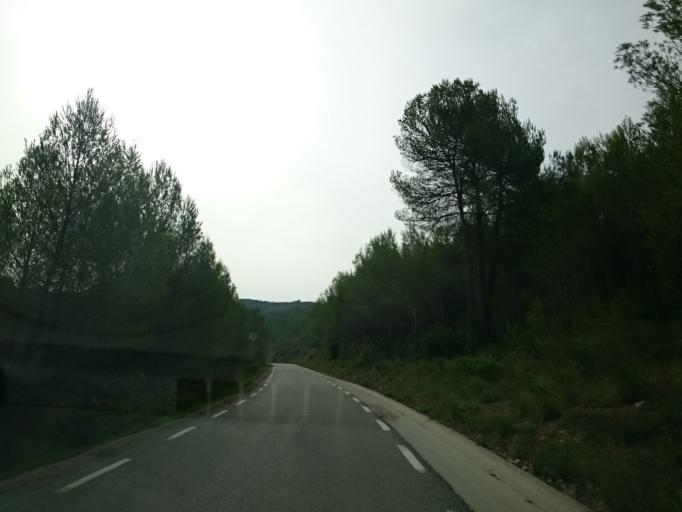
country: ES
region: Catalonia
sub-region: Provincia de Barcelona
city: Olivella
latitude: 41.3103
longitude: 1.7977
